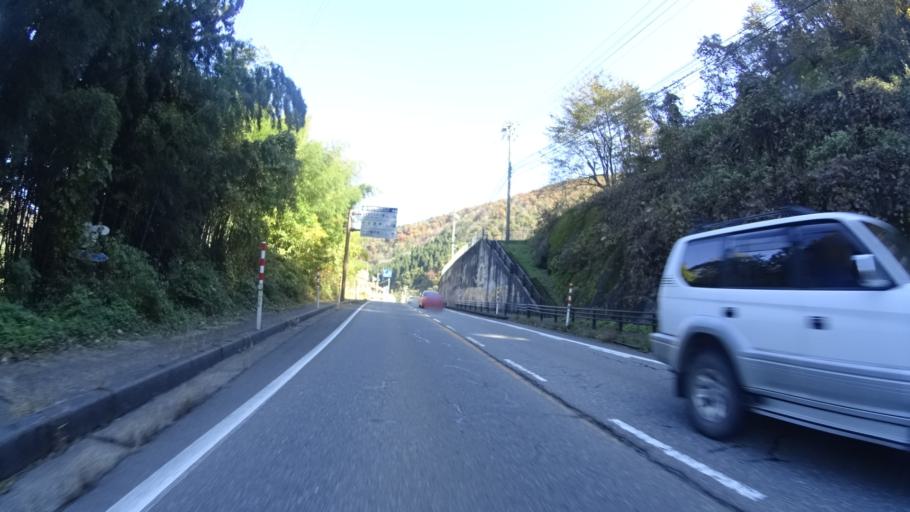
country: JP
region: Ishikawa
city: Tsurugi-asahimachi
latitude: 36.4020
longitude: 136.6298
